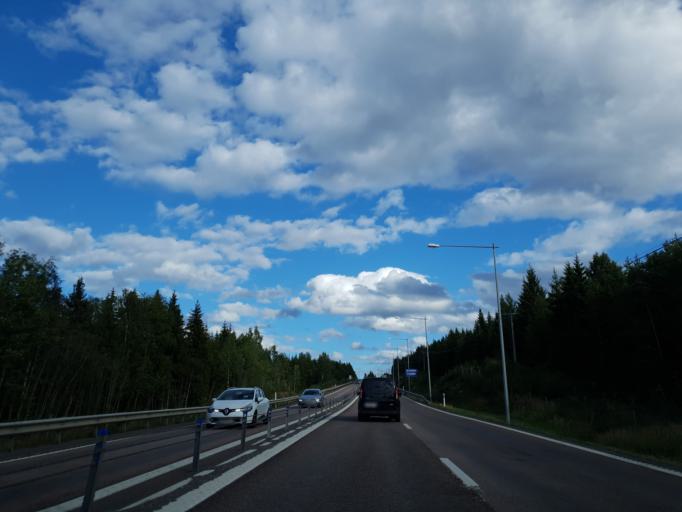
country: SE
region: Vaesternorrland
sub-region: Haernoesands Kommun
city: Haernoesand
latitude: 62.6574
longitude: 17.8687
